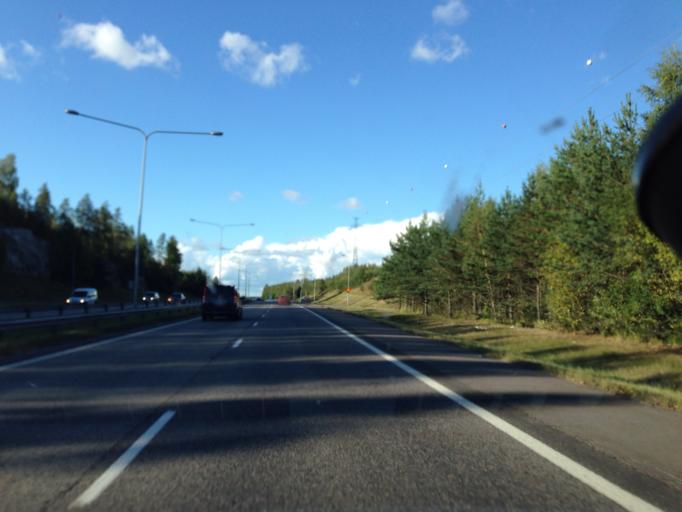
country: FI
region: Uusimaa
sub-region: Helsinki
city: Vantaa
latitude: 60.3251
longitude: 24.9980
